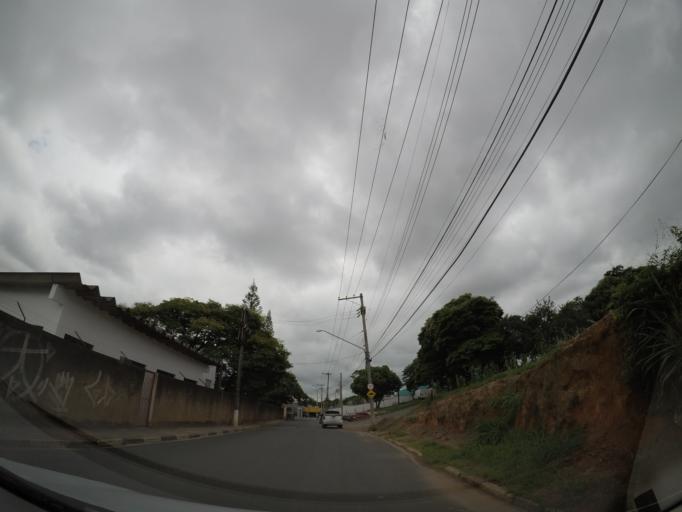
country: BR
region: Sao Paulo
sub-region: Louveira
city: Louveira
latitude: -23.0887
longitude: -46.9824
